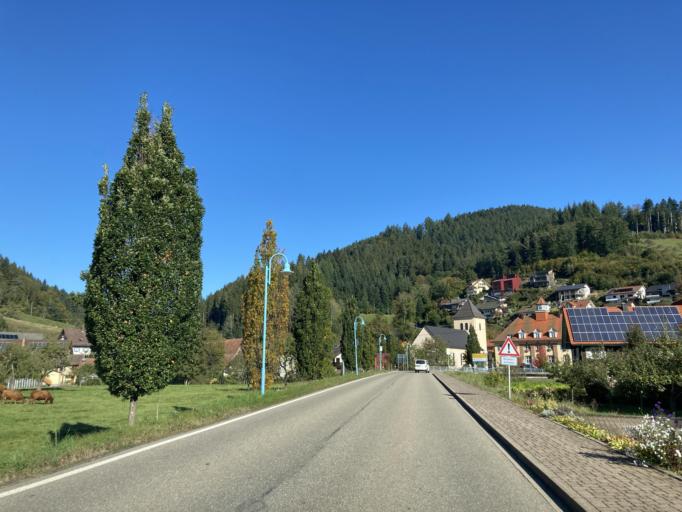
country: DE
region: Baden-Wuerttemberg
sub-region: Freiburg Region
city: Oberwolfach
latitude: 48.3432
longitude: 8.2250
